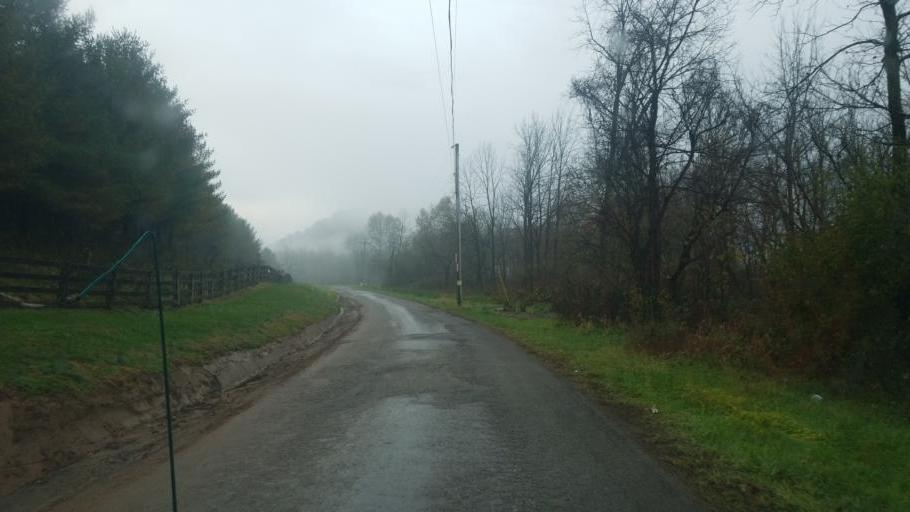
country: US
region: Ohio
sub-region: Athens County
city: Glouster
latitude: 39.4435
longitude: -81.9223
